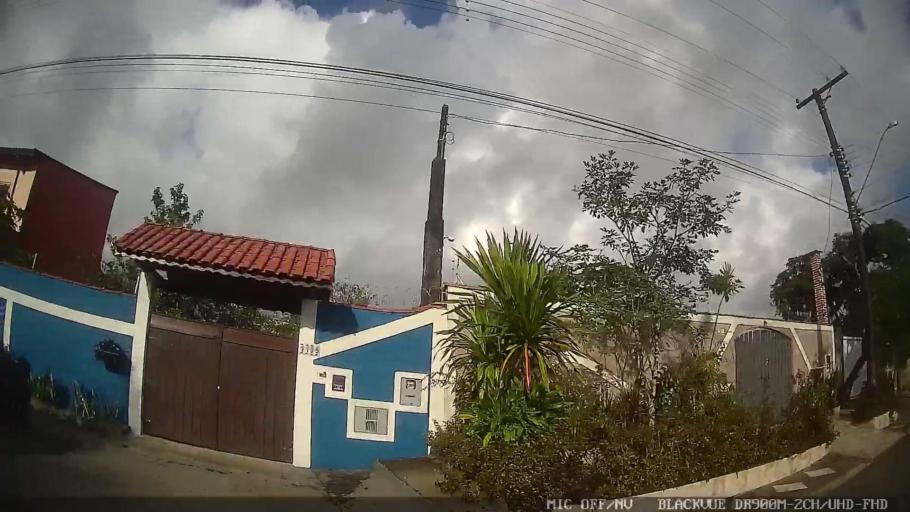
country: BR
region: Sao Paulo
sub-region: Itanhaem
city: Itanhaem
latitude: -24.1894
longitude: -46.8616
